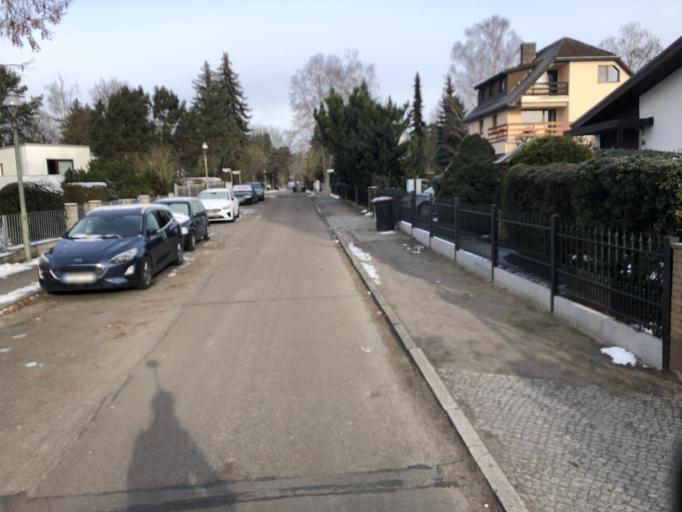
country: DE
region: Berlin
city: Hermsdorf
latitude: 52.6239
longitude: 13.3085
